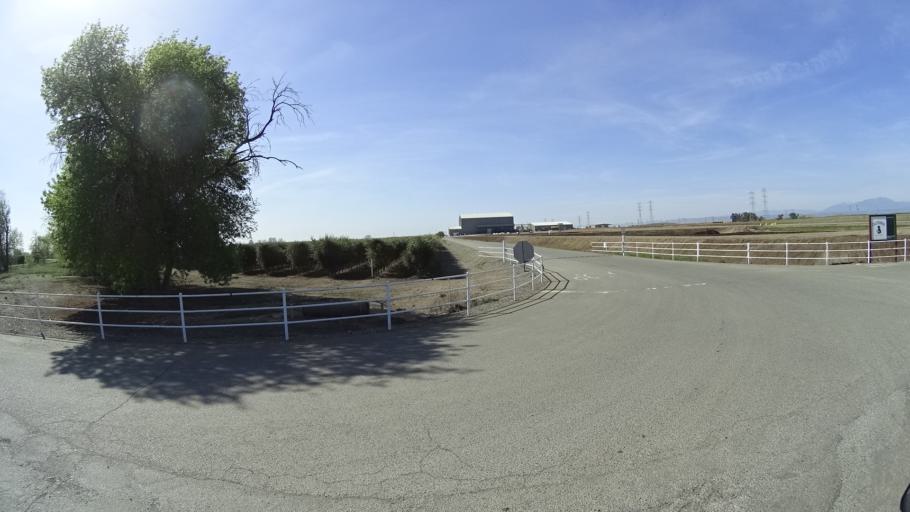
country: US
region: California
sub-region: Glenn County
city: Willows
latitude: 39.6116
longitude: -122.2609
